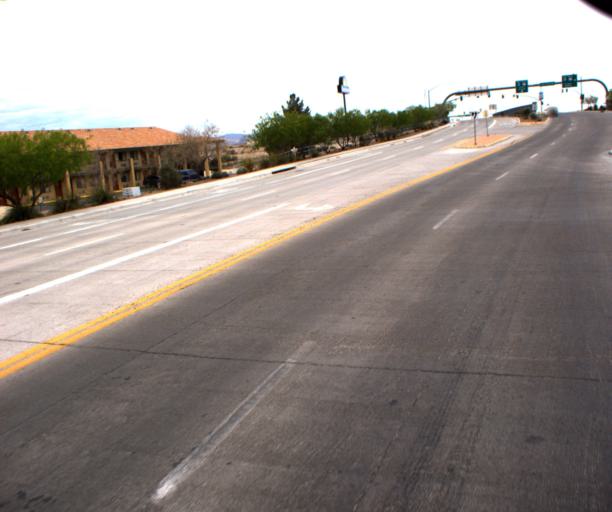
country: US
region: Arizona
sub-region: Cochise County
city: Willcox
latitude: 32.2649
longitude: -109.8418
